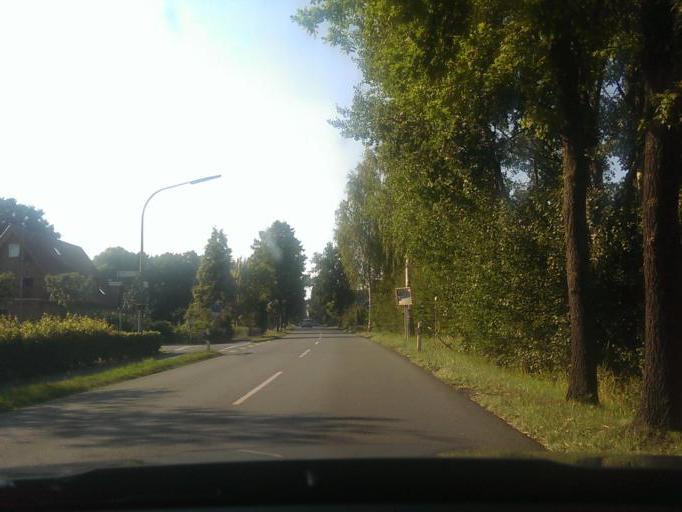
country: DE
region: North Rhine-Westphalia
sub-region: Regierungsbezirk Detmold
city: Delbruck
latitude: 51.7482
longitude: 8.5822
